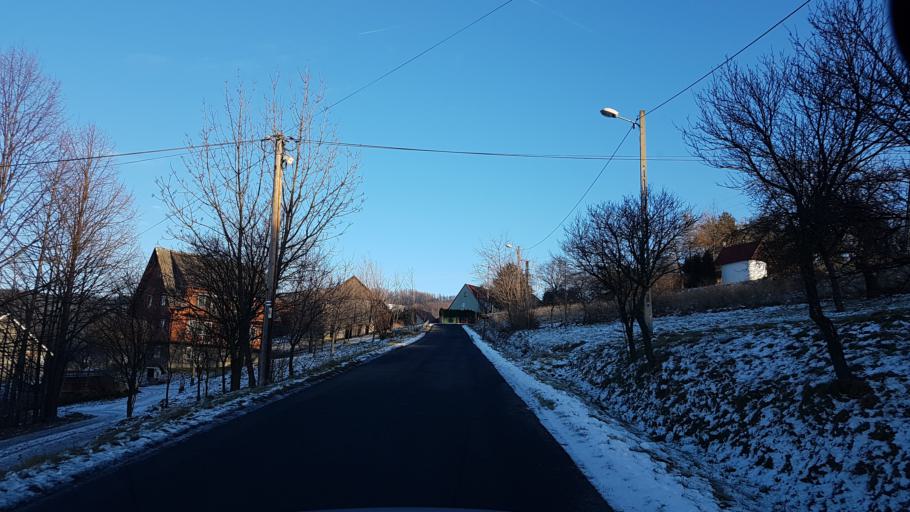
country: PL
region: Lesser Poland Voivodeship
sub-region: Powiat nowosadecki
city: Rytro
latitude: 49.5147
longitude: 20.6657
